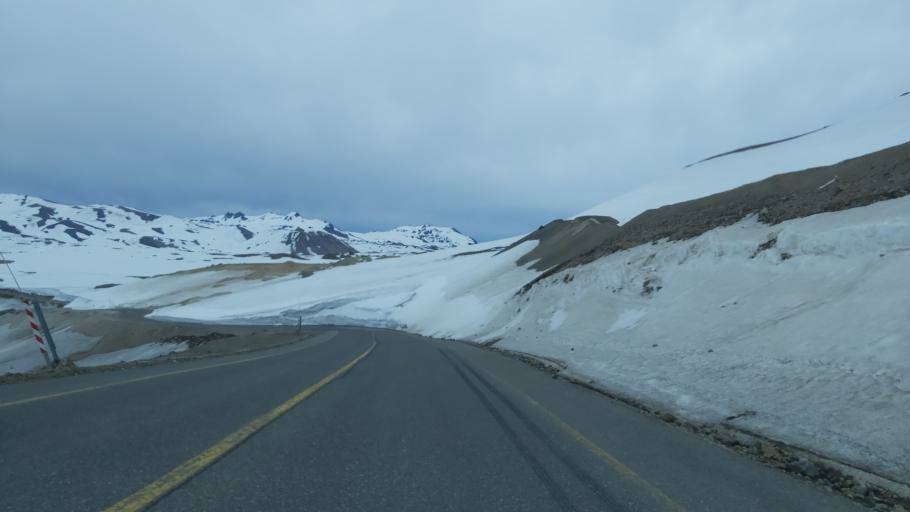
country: CL
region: Maule
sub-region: Provincia de Linares
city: Colbun
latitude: -36.0174
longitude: -70.5181
